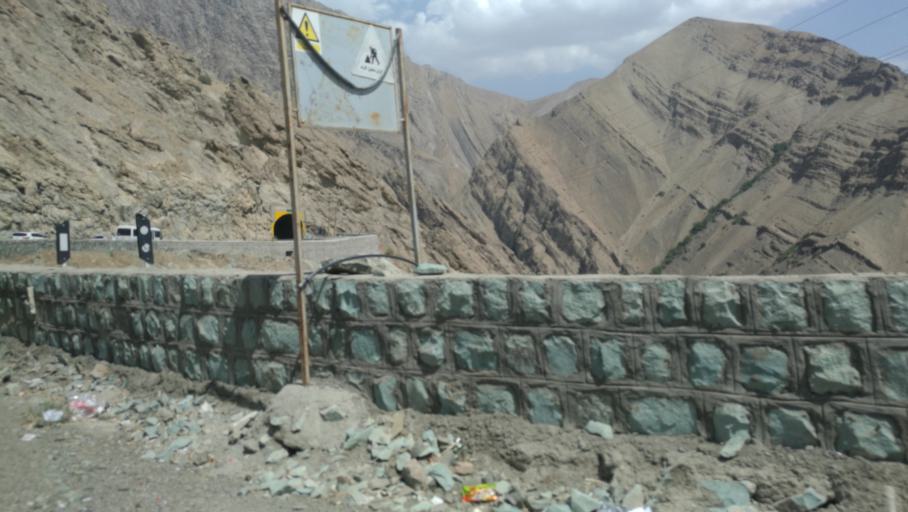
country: IR
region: Alborz
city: Karaj
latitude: 35.9491
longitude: 51.0849
